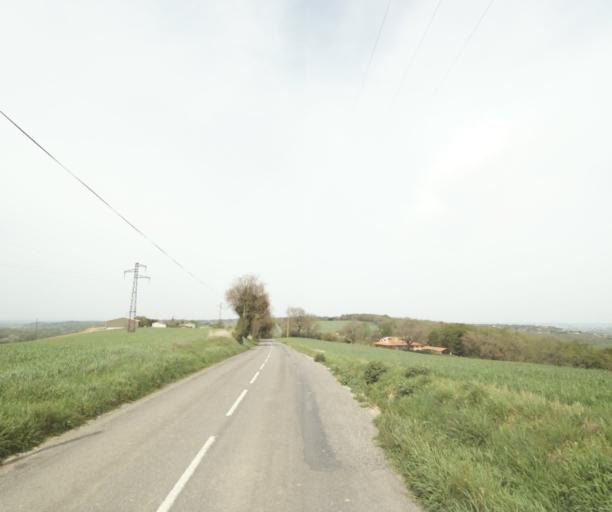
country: FR
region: Midi-Pyrenees
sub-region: Departement de la Haute-Garonne
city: Pechabou
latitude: 43.4921
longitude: 1.4935
